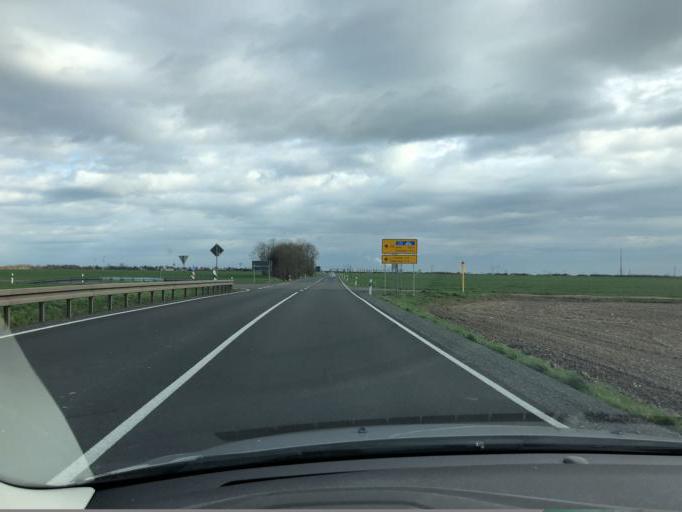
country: DE
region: Saxony
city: Markranstadt
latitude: 51.2817
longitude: 12.2538
